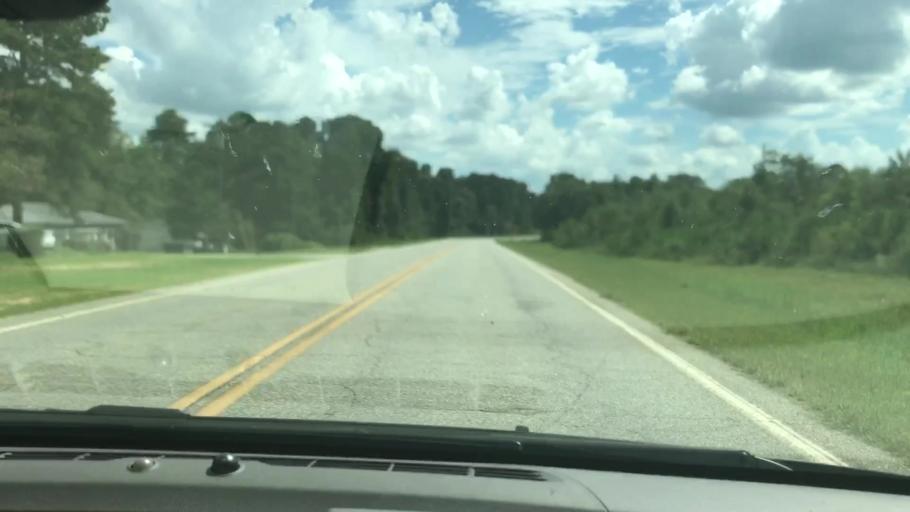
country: US
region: Georgia
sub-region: Clay County
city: Fort Gaines
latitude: 31.6738
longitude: -85.0467
